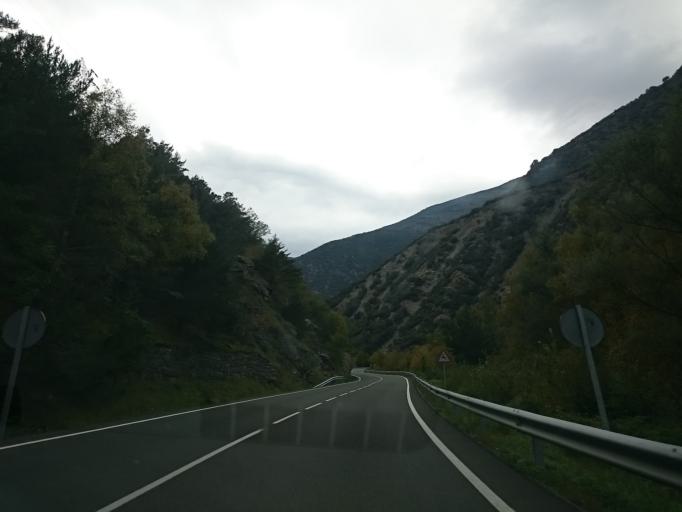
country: ES
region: Catalonia
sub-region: Provincia de Lleida
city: Farrera
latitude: 42.4668
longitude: 1.1963
